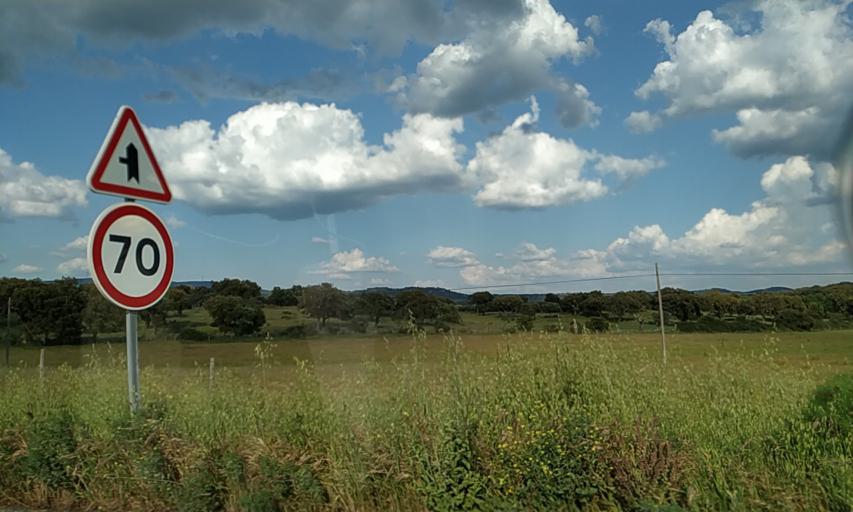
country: PT
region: Portalegre
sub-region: Portalegre
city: Portalegre
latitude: 39.2530
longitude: -7.4477
